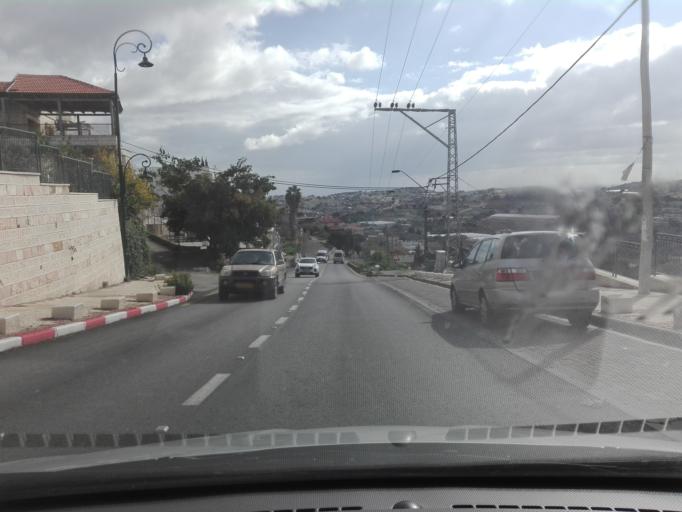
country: IL
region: Haifa
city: Daliyat el Karmil
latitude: 32.7163
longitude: 35.0674
